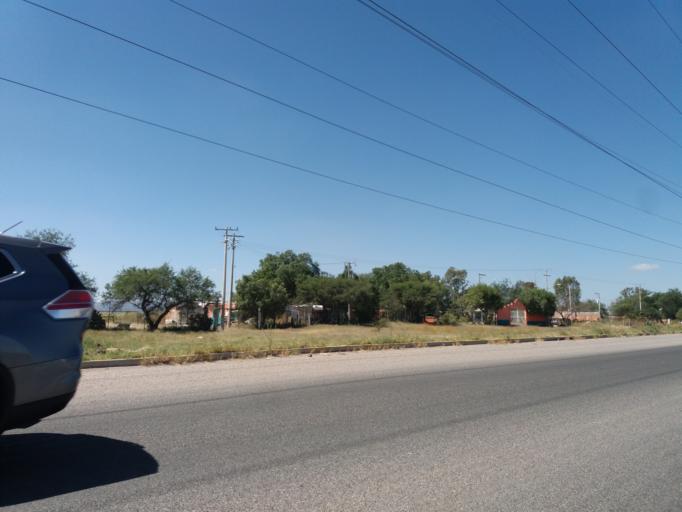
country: MX
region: Aguascalientes
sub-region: Aguascalientes
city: San Sebastian [Fraccionamiento]
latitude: 21.8107
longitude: -102.2921
